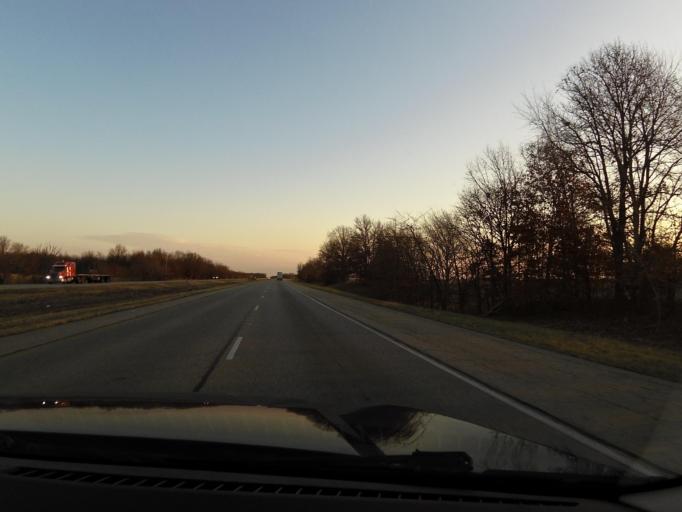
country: US
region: Illinois
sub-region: Marion County
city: Salem
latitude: 38.6979
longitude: -88.9590
